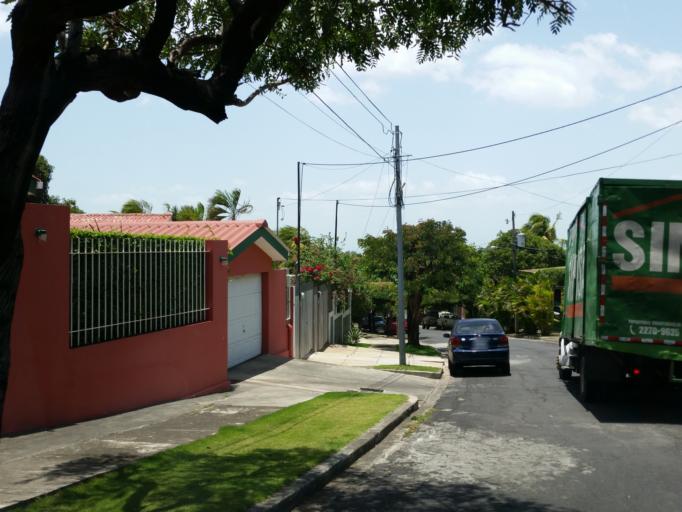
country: NI
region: Managua
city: Managua
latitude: 12.1148
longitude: -86.2776
